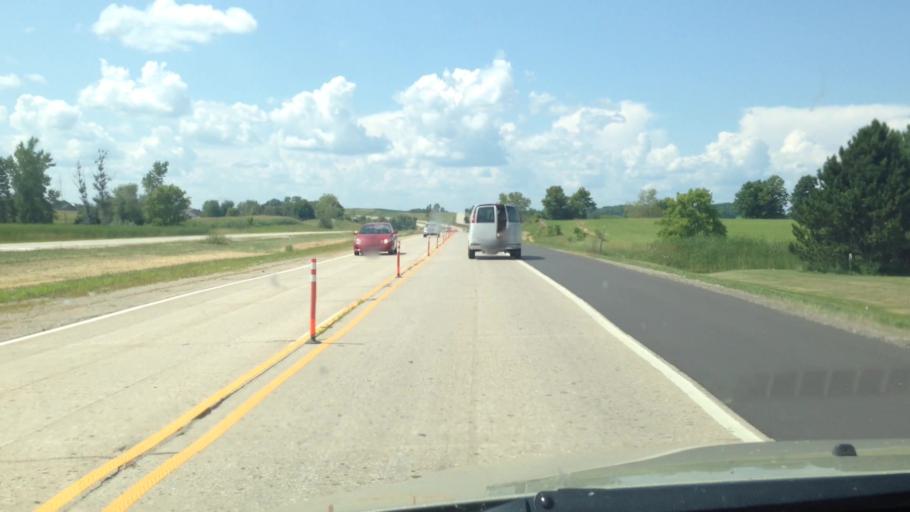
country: US
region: Wisconsin
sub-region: Shawano County
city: Bonduel
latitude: 44.7130
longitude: -88.3863
